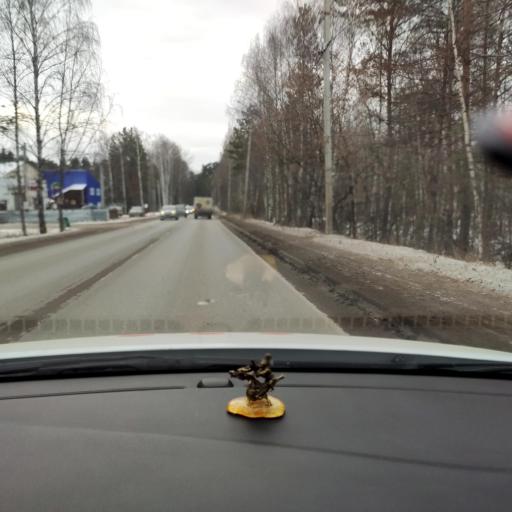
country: RU
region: Tatarstan
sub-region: Zelenodol'skiy Rayon
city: Zelenodolsk
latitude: 55.8658
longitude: 48.5381
